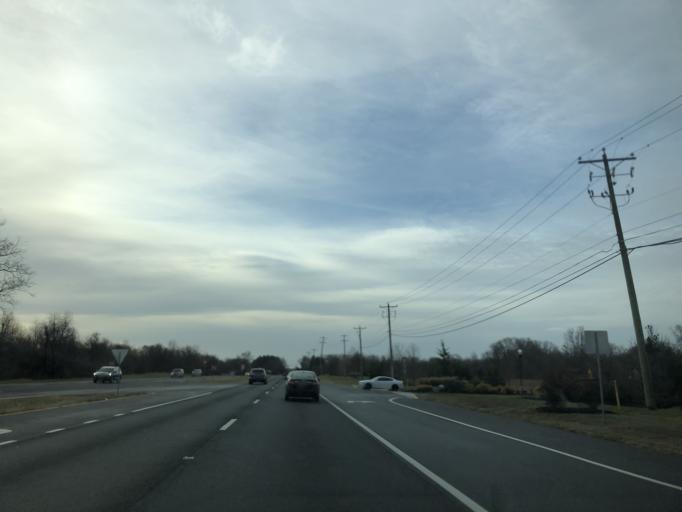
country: US
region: Delaware
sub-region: New Castle County
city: Middletown
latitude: 39.4837
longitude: -75.6510
